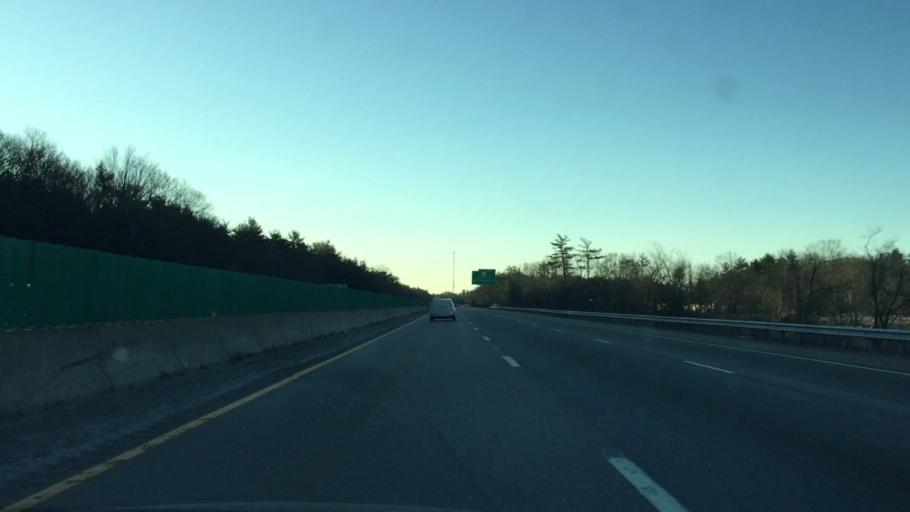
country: US
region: Massachusetts
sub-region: Plymouth County
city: West Bridgewater
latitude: 42.0339
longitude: -71.0523
